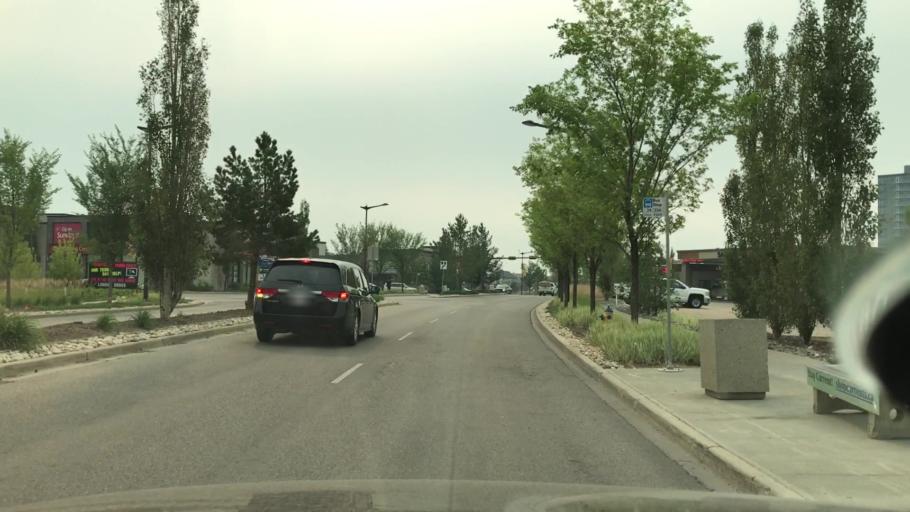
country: CA
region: Alberta
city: Devon
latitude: 53.4371
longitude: -113.6011
